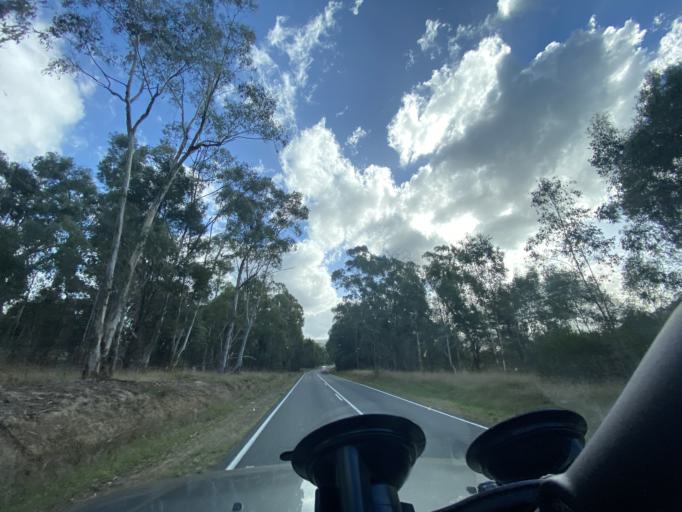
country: AU
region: Victoria
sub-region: Murrindindi
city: Kinglake West
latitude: -37.3224
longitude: 145.3098
